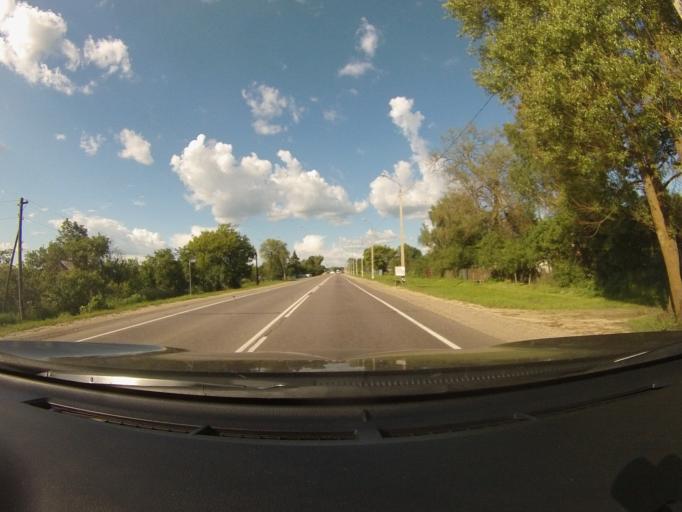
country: RU
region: Tula
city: Bol'shoye Skuratovo
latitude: 53.4269
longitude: 36.7945
